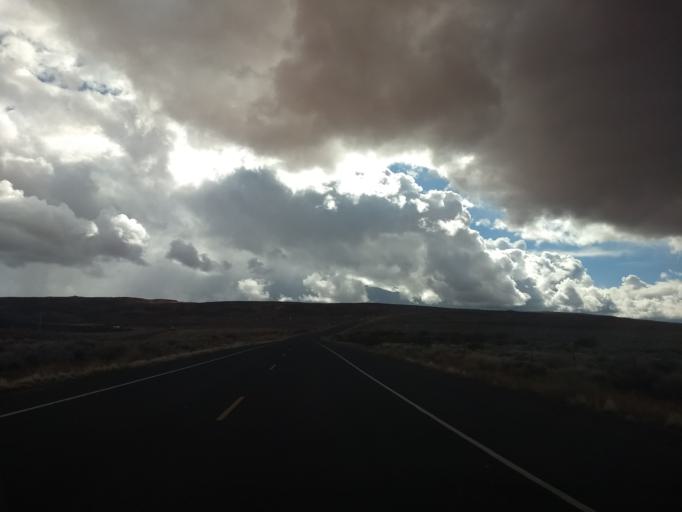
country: US
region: Utah
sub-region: Washington County
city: Washington
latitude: 37.1115
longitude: -113.3929
